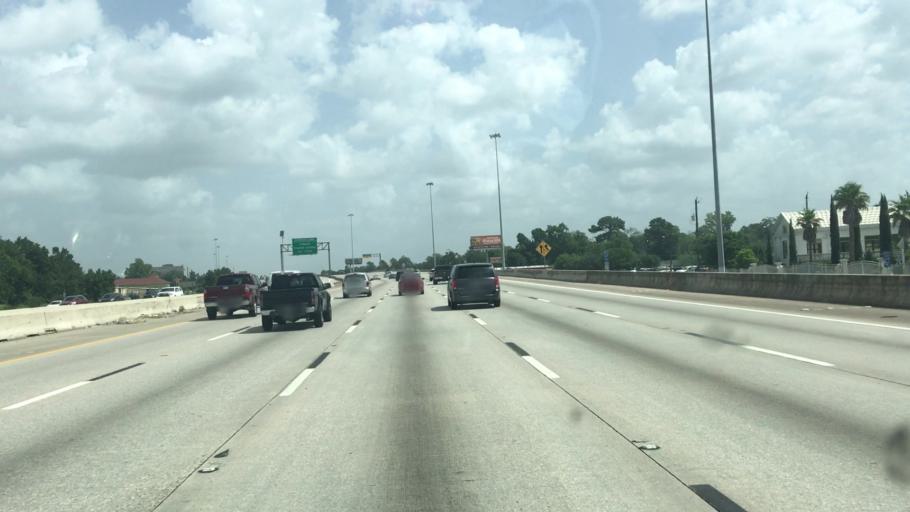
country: US
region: Texas
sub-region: Harris County
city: Houston
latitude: 29.8353
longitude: -95.3338
